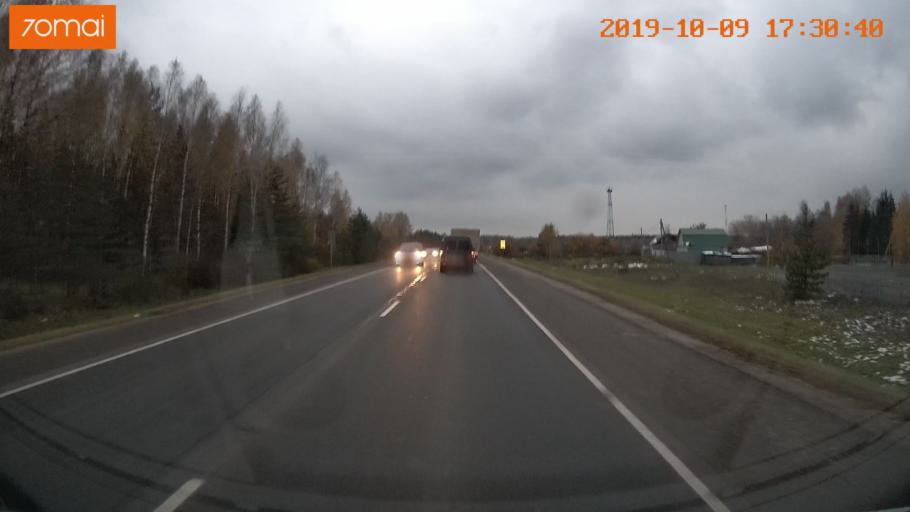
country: RU
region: Ivanovo
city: Bogorodskoye
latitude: 57.1411
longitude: 41.0471
